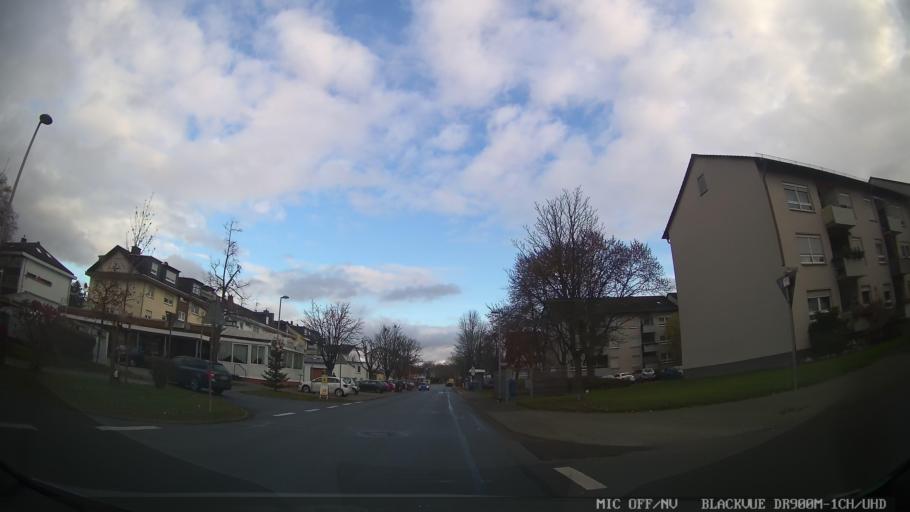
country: DE
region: Hesse
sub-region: Regierungsbezirk Darmstadt
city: Nauheim
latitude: 49.9614
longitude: 8.4547
